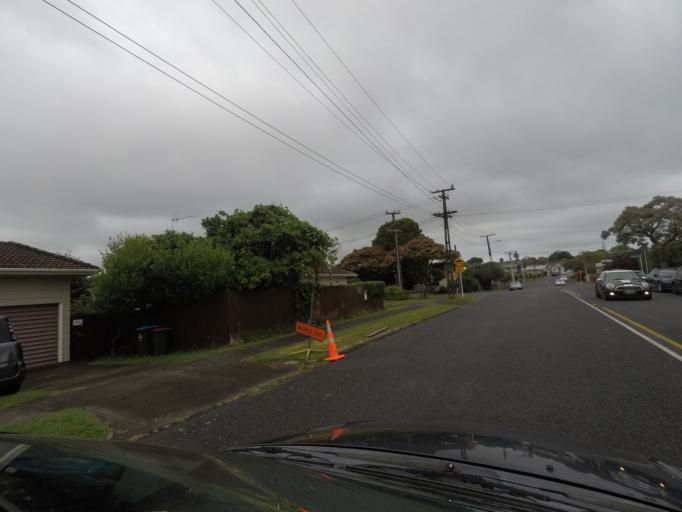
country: NZ
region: Auckland
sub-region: Auckland
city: Auckland
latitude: -36.8891
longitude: 174.7322
